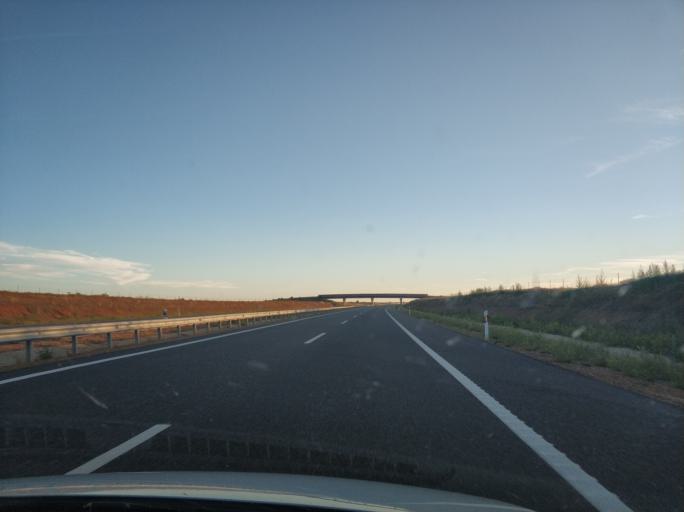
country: ES
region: Castille and Leon
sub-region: Provincia de Zamora
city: Castrogonzalo
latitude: 41.9554
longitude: -5.6177
